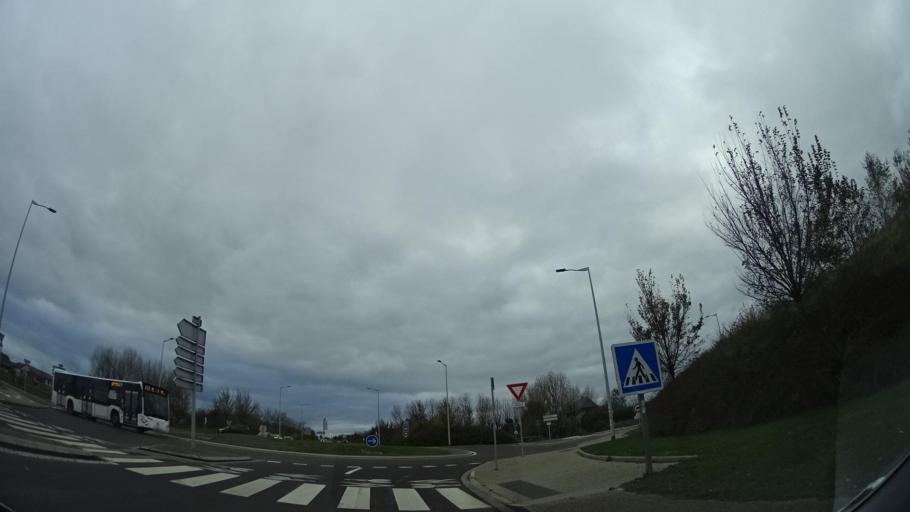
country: FR
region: Haute-Normandie
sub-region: Departement de la Seine-Maritime
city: Octeville-sur-Mer
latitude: 49.5318
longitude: 0.1040
